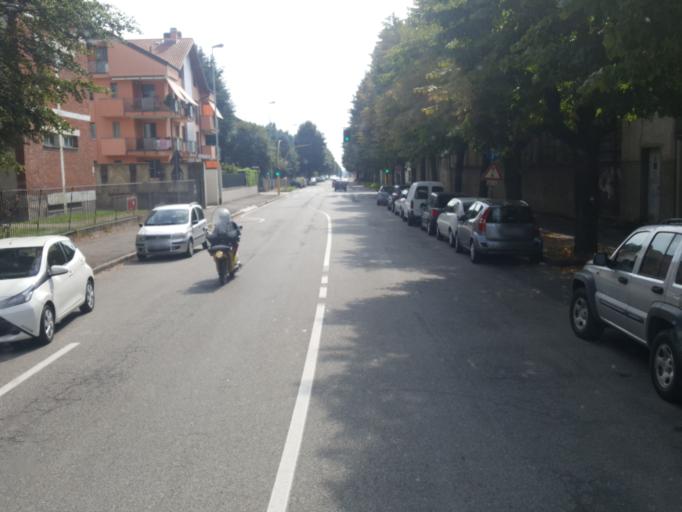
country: IT
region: Lombardy
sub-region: Citta metropolitana di Milano
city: Abbiategrasso
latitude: 45.3935
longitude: 8.9143
